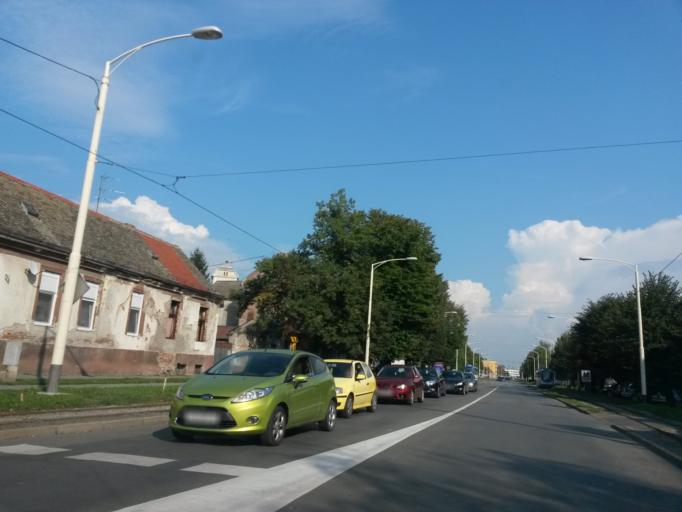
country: HR
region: Osjecko-Baranjska
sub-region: Grad Osijek
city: Osijek
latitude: 45.5549
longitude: 18.7204
